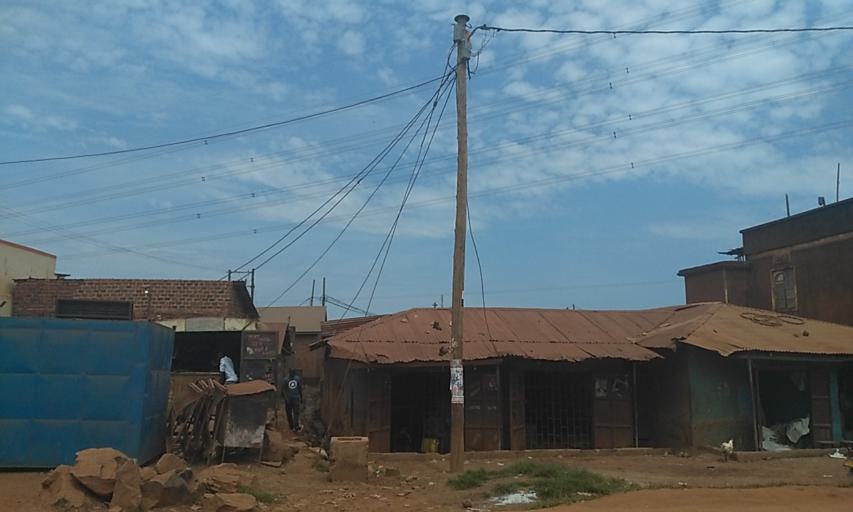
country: UG
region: Central Region
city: Kampala Central Division
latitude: 0.2970
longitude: 32.5261
